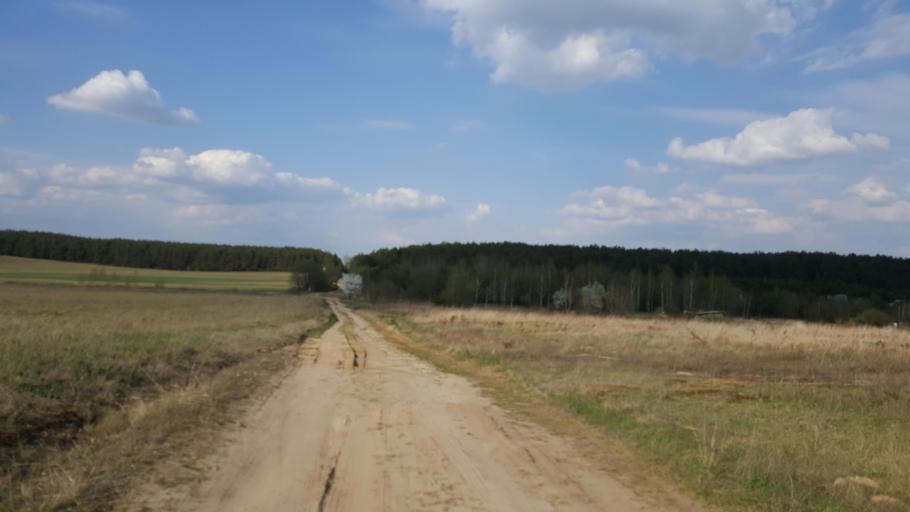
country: BY
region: Brest
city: Kamyanyets
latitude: 52.3746
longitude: 23.8368
